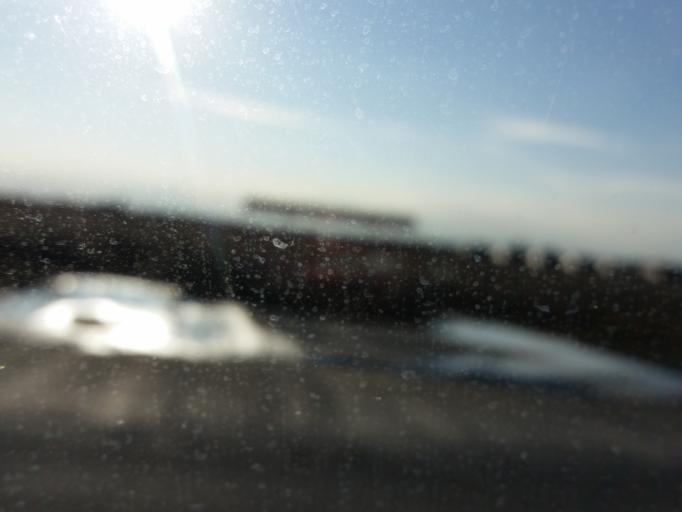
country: US
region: North Dakota
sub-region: Grand Forks County
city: Grand Forks
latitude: 47.8651
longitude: -97.0344
